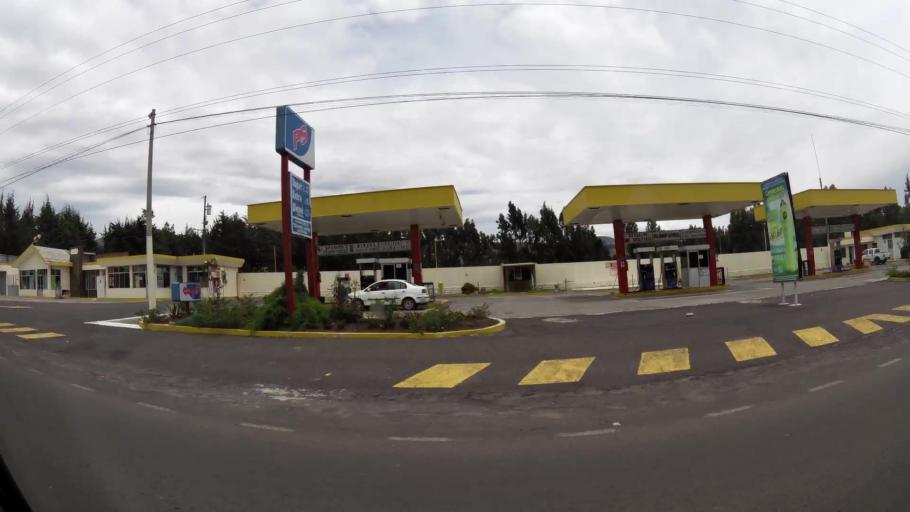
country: EC
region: Cotopaxi
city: San Miguel de Salcedo
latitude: -1.0089
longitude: -78.5932
